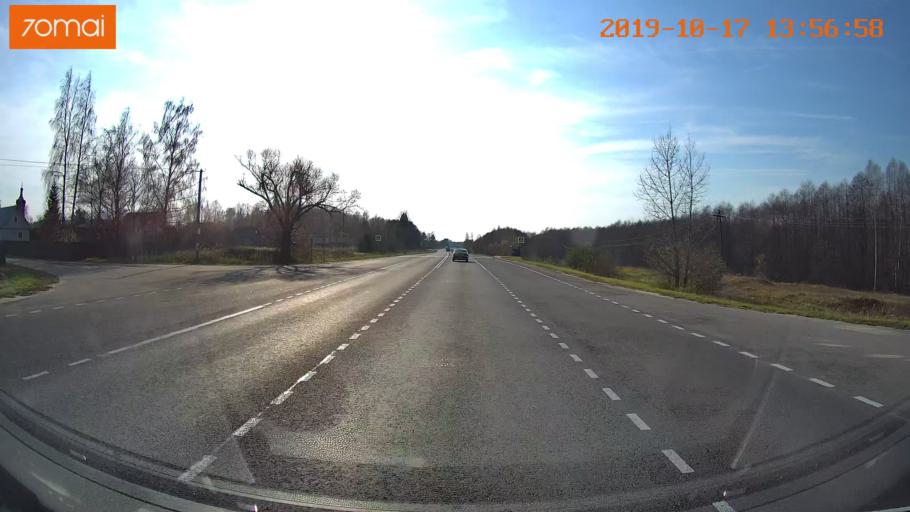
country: RU
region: Rjazan
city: Spas-Klepiki
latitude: 55.1475
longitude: 40.2547
